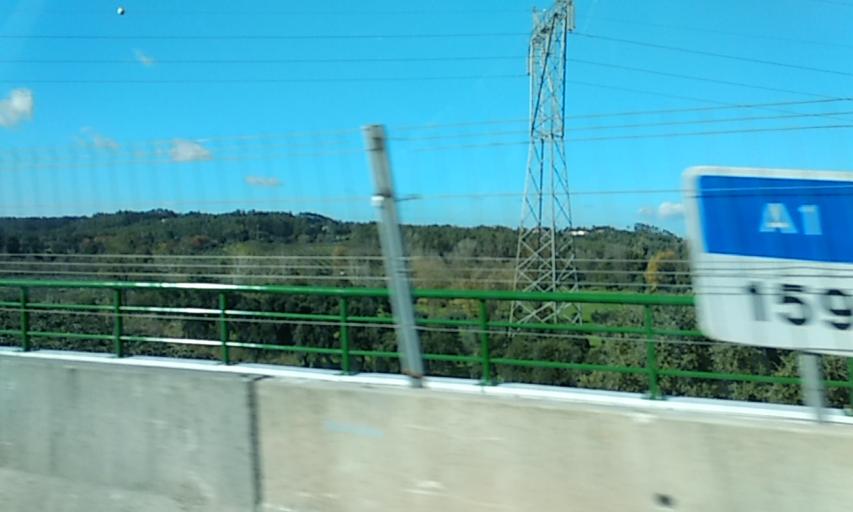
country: PT
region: Leiria
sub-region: Pombal
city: Pombal
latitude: 39.9741
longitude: -8.6404
